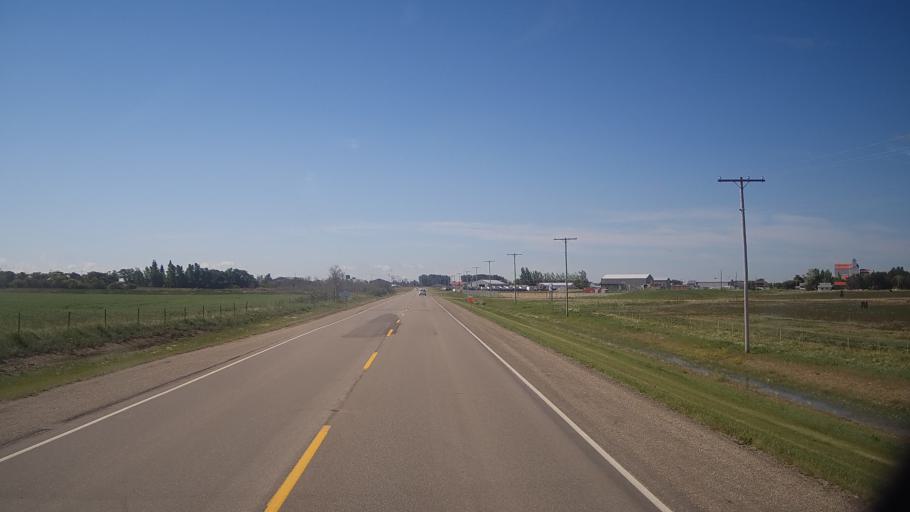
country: CA
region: Saskatchewan
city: Watrous
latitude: 51.6759
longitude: -105.4517
